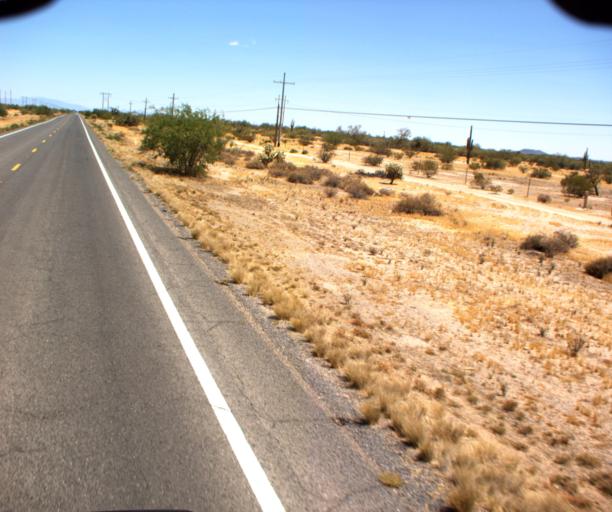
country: US
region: Arizona
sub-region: Pinal County
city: Florence
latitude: 32.9334
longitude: -111.3096
